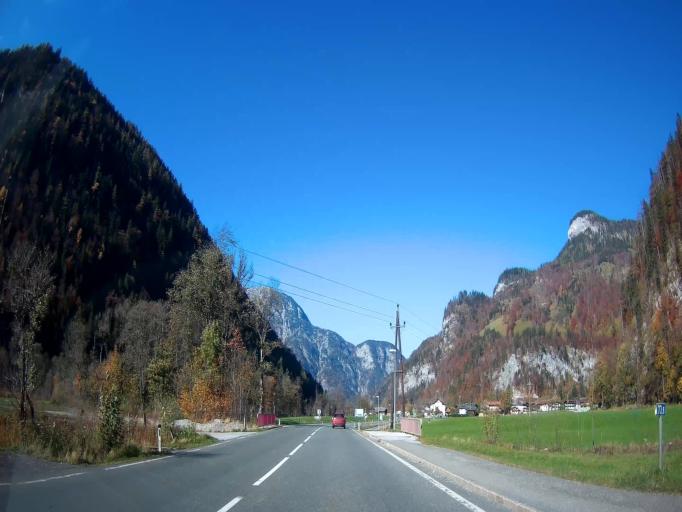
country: AT
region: Salzburg
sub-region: Politischer Bezirk Zell am See
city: Sankt Martin bei Lofer
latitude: 47.5165
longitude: 12.7576
